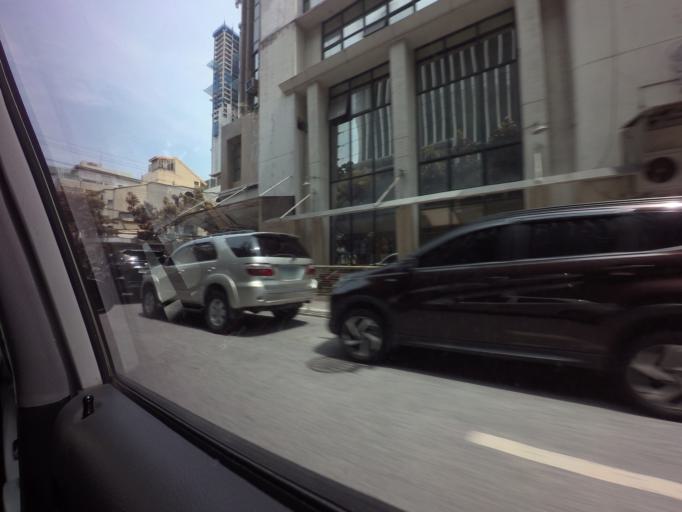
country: PH
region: Metro Manila
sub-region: City of Manila
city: Port Area
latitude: 14.5736
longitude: 120.9891
